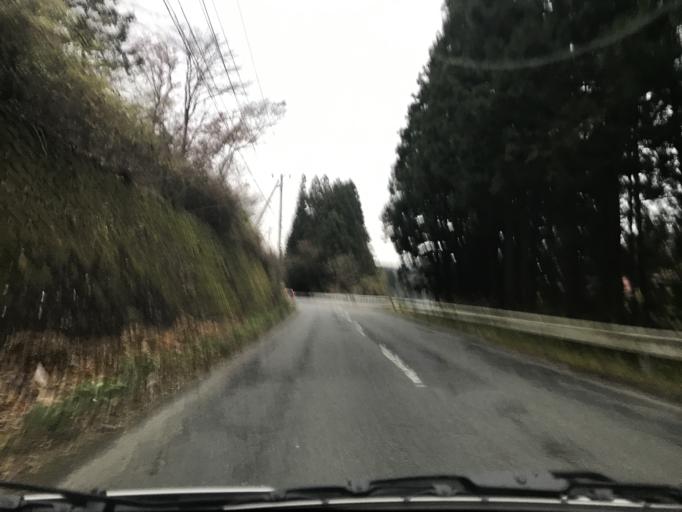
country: JP
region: Iwate
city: Mizusawa
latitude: 39.0356
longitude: 141.3409
